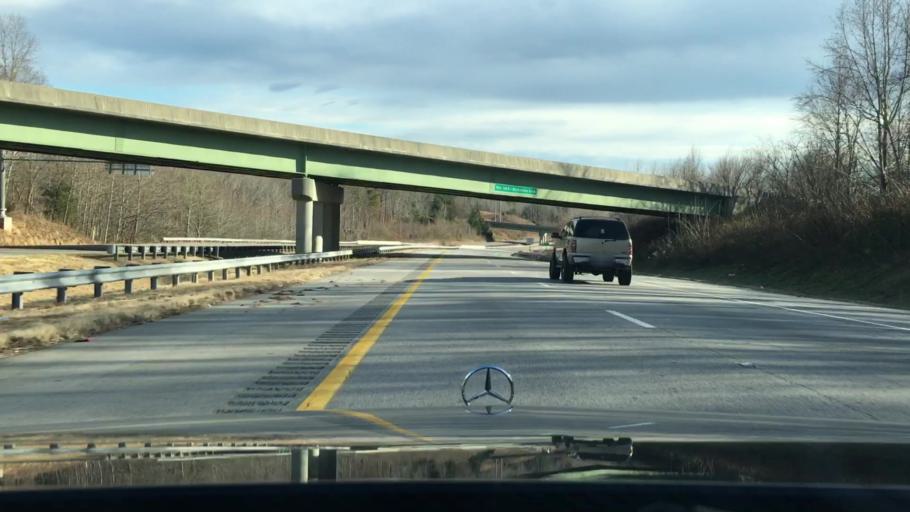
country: US
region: Virginia
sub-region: City of Danville
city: Danville
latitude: 36.6118
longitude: -79.3614
